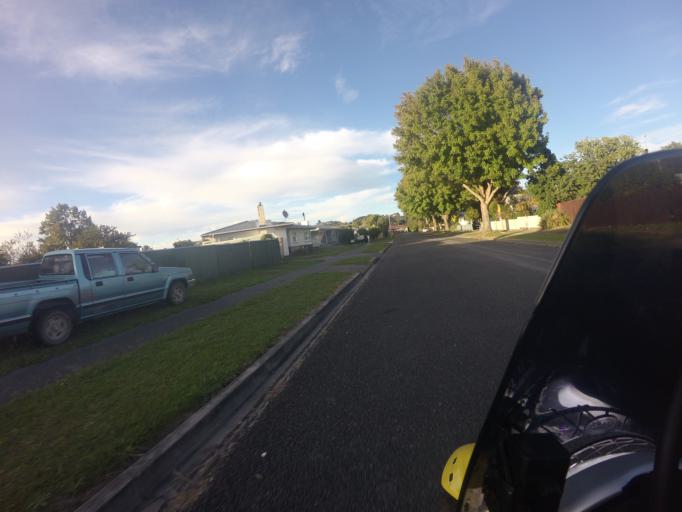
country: NZ
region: Gisborne
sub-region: Gisborne District
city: Gisborne
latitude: -38.6733
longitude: 178.0492
